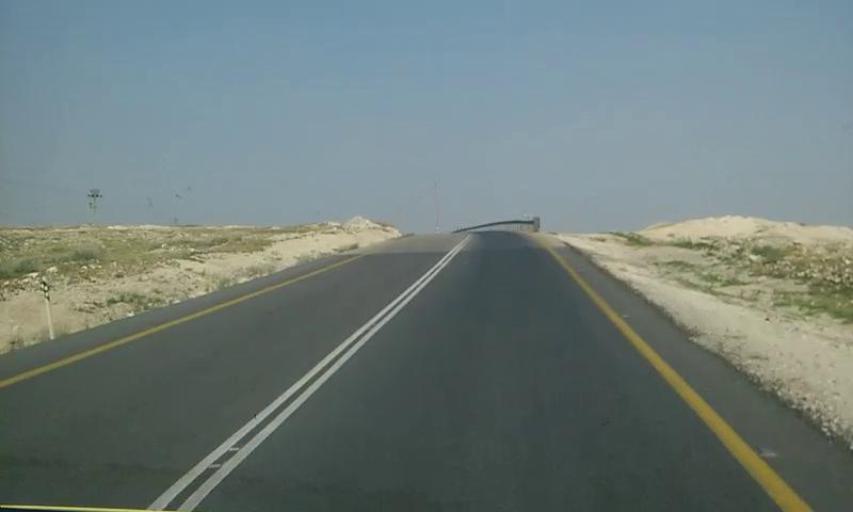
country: PS
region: West Bank
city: Al `Awja
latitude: 31.9706
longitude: 35.4706
